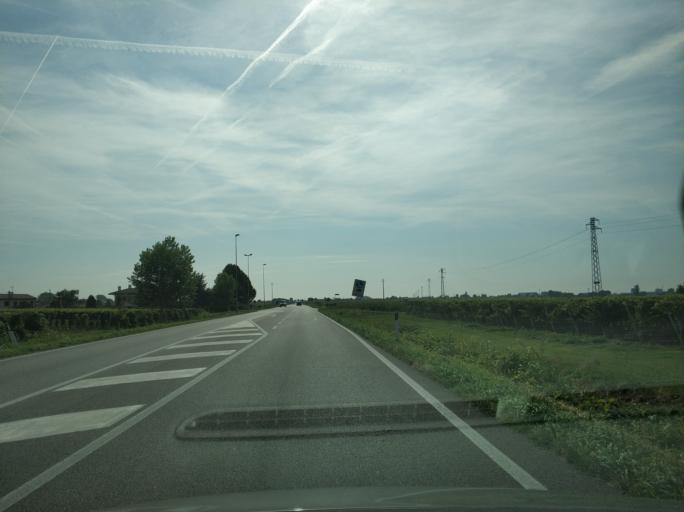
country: IT
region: Veneto
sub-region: Provincia di Padova
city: Conselve
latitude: 45.2143
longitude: 11.8660
